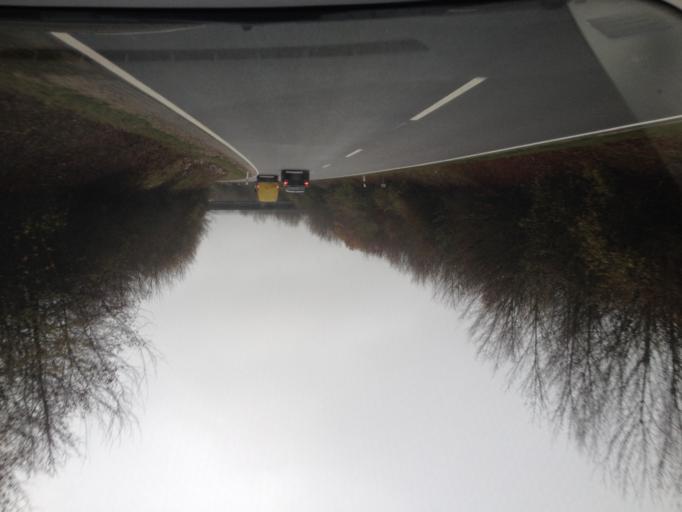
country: DE
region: Bavaria
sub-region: Regierungsbezirk Mittelfranken
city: Heroldsberg
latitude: 49.5407
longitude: 11.1661
